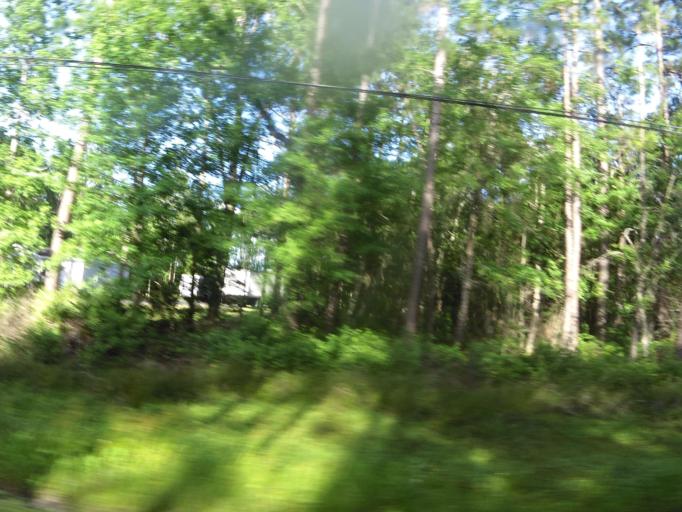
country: US
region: Florida
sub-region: Nassau County
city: Nassau Village-Ratliff
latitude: 30.4719
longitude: -81.7844
